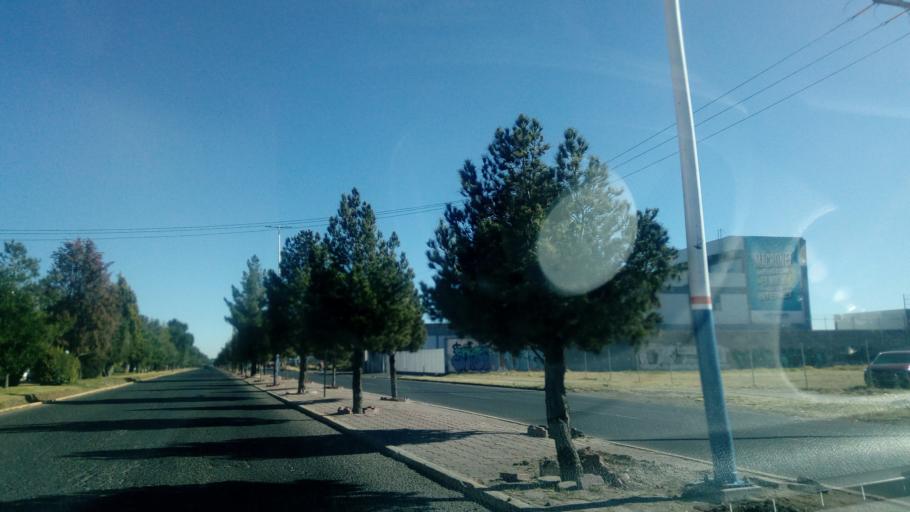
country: MX
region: Durango
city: Victoria de Durango
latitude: 24.0546
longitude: -104.6151
